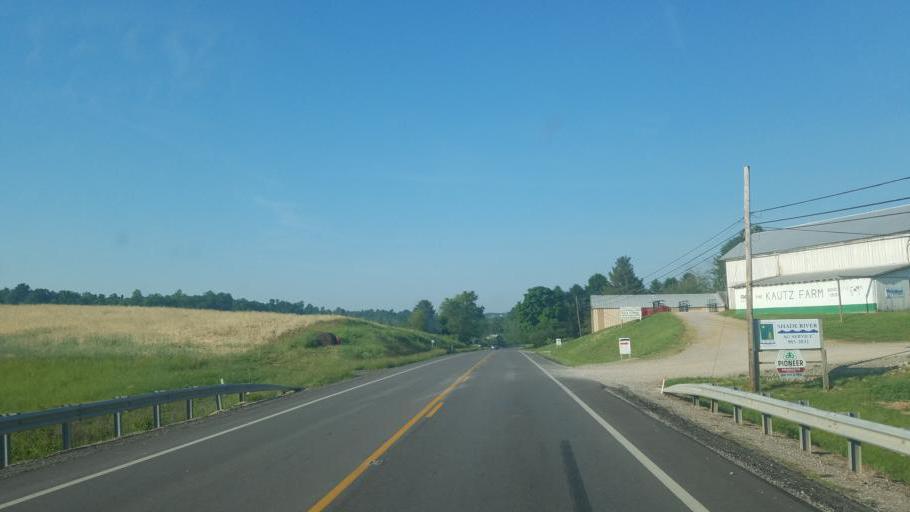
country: US
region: West Virginia
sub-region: Mason County
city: New Haven
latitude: 39.0768
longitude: -81.9303
